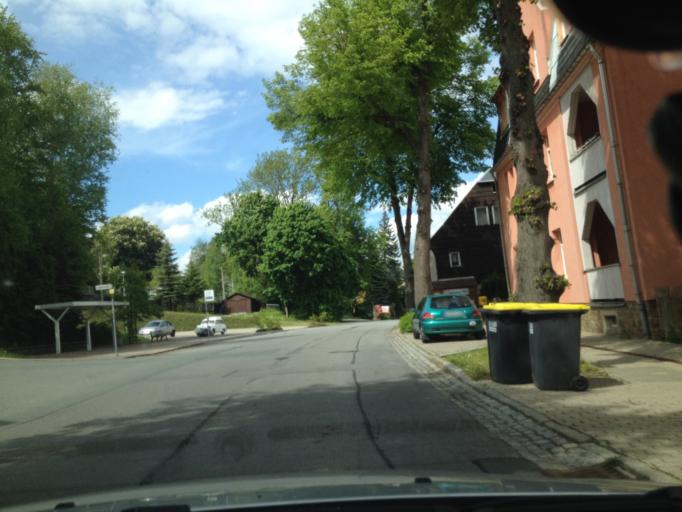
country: DE
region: Saxony
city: Crottendorf
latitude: 50.5324
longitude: 12.9946
